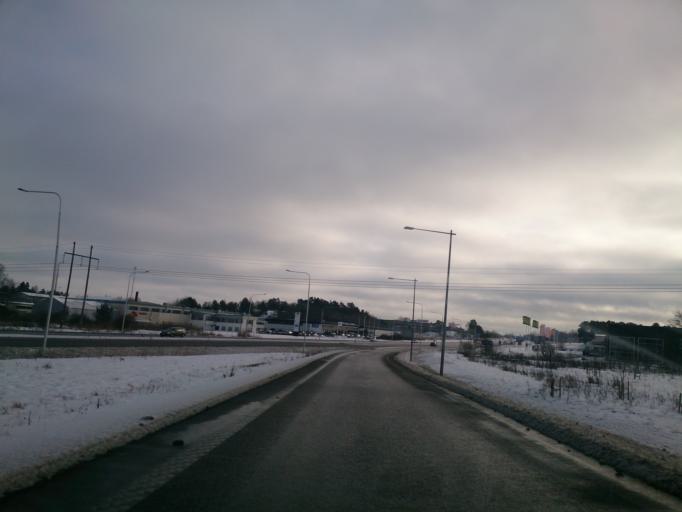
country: SE
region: OEstergoetland
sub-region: Norrkopings Kommun
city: Norrkoping
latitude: 58.6249
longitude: 16.1580
